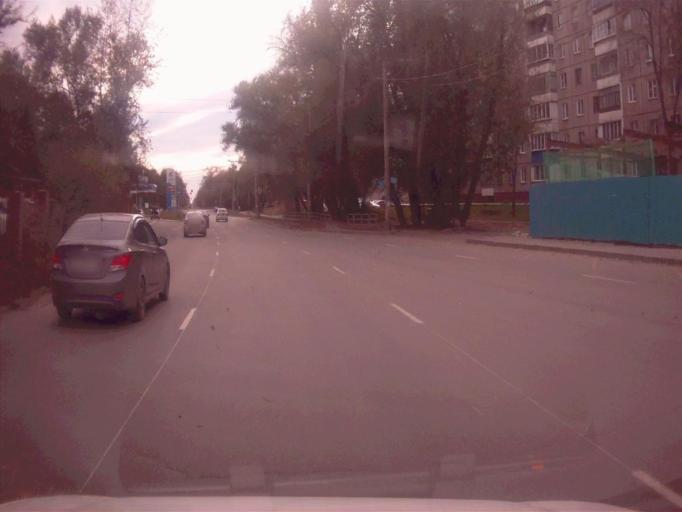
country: RU
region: Chelyabinsk
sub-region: Gorod Chelyabinsk
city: Chelyabinsk
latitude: 55.1250
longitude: 61.4753
